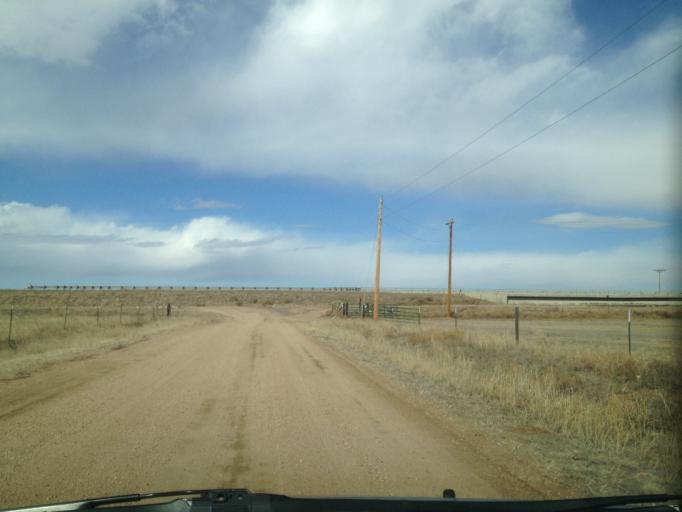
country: US
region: Colorado
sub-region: Weld County
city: Keenesburg
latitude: 40.2902
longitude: -104.2555
